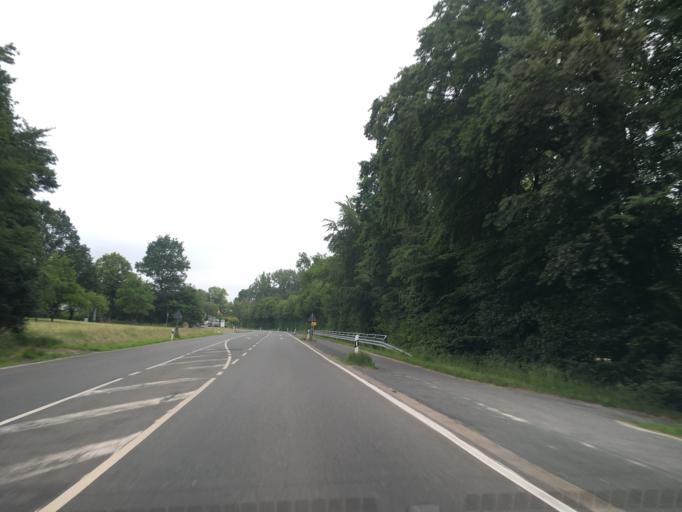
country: DE
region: North Rhine-Westphalia
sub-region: Regierungsbezirk Munster
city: Steinfurt
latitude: 52.1375
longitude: 7.3435
